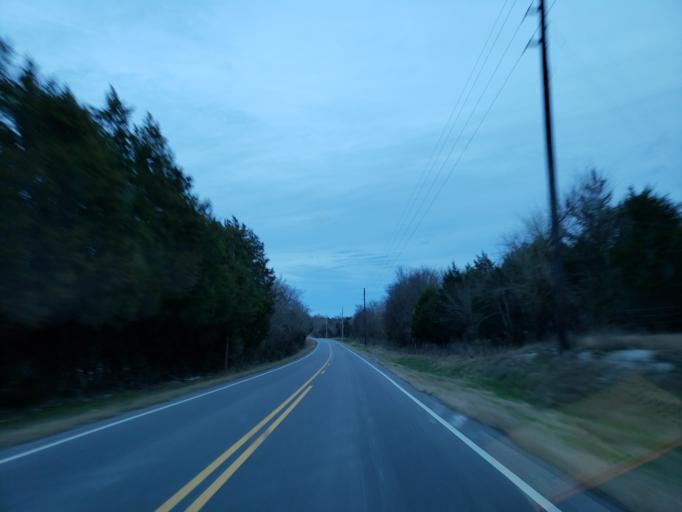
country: US
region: Alabama
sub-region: Sumter County
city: Livingston
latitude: 32.8111
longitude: -88.2677
